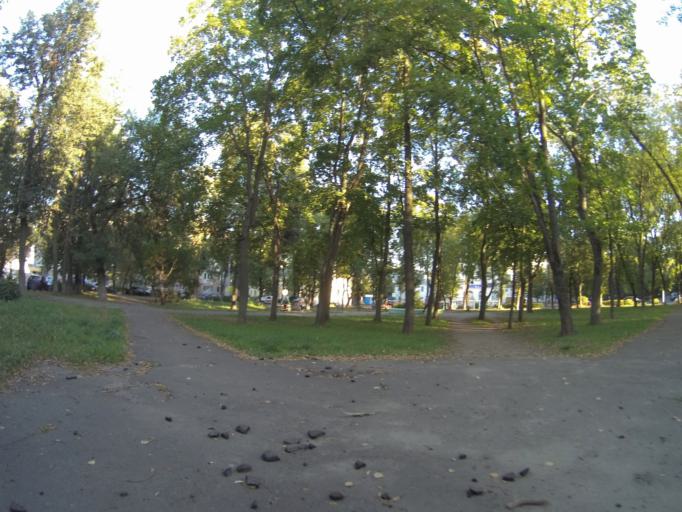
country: RU
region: Vladimir
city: Vladimir
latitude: 56.1490
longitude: 40.3831
